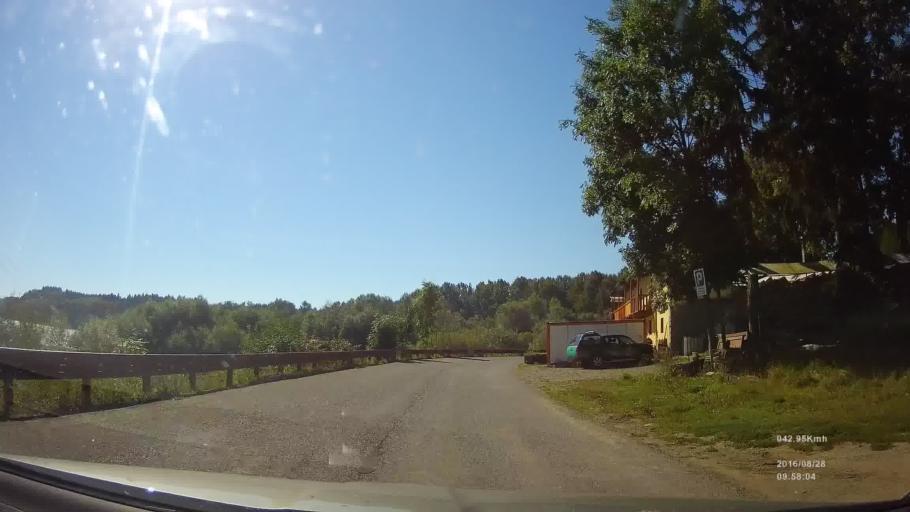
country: SK
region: Zilinsky
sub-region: Okres Liptovsky Mikulas
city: Liptovsky Mikulas
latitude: 49.1175
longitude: 19.4801
